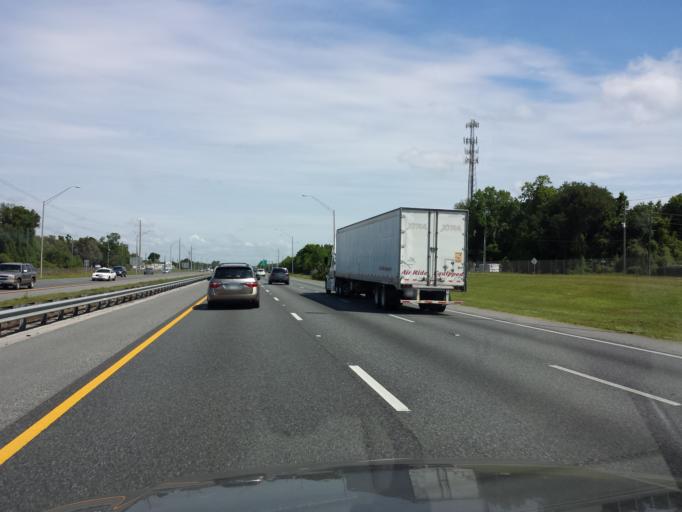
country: US
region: Florida
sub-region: Marion County
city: Ocala
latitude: 29.1965
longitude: -82.1846
